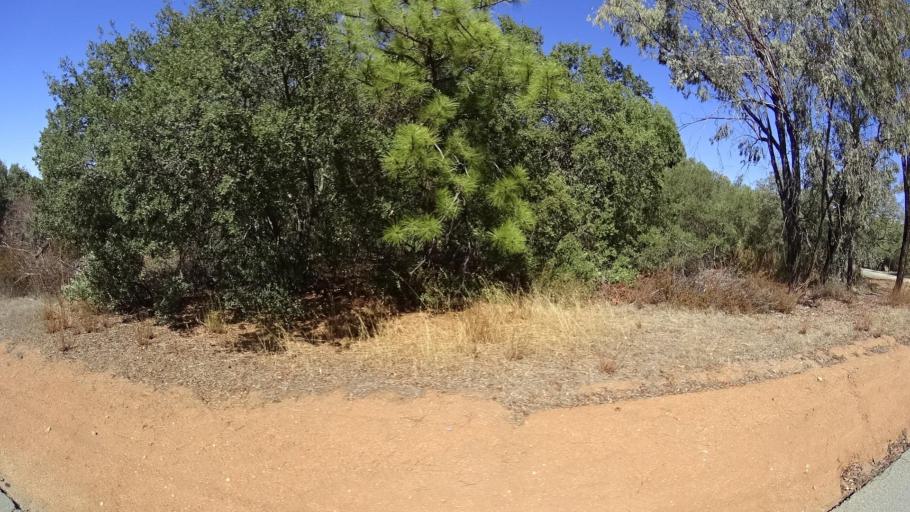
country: US
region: California
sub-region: San Diego County
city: Descanso
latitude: 32.7949
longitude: -116.6572
